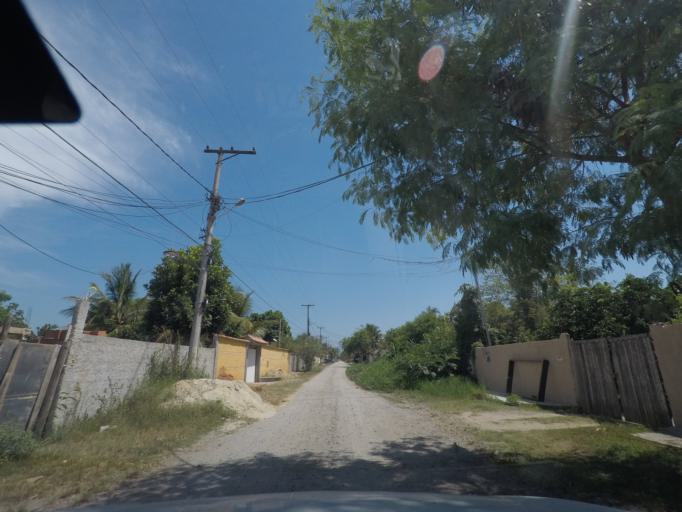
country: BR
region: Rio de Janeiro
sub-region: Marica
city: Marica
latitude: -22.9525
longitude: -42.9595
